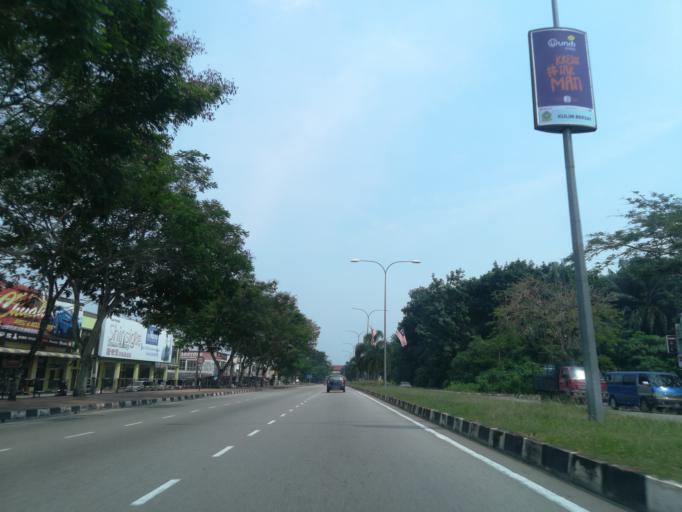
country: MY
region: Kedah
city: Kulim
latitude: 5.4123
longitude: 100.5439
